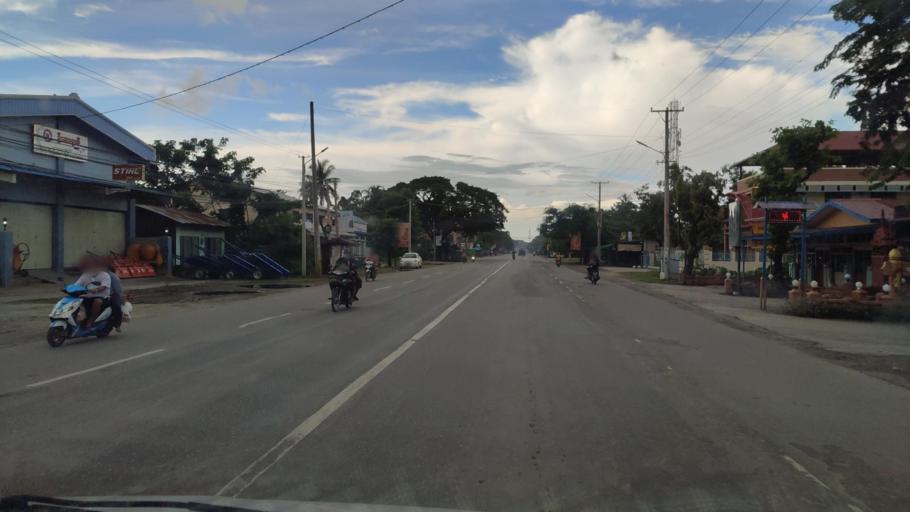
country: MM
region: Bago
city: Taungoo
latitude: 18.9197
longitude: 96.4455
